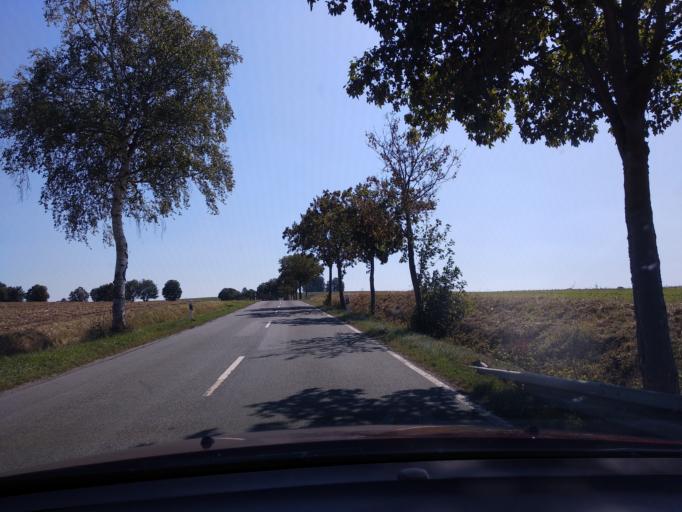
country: DE
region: North Rhine-Westphalia
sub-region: Regierungsbezirk Detmold
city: Willebadessen
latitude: 51.6575
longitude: 9.0686
